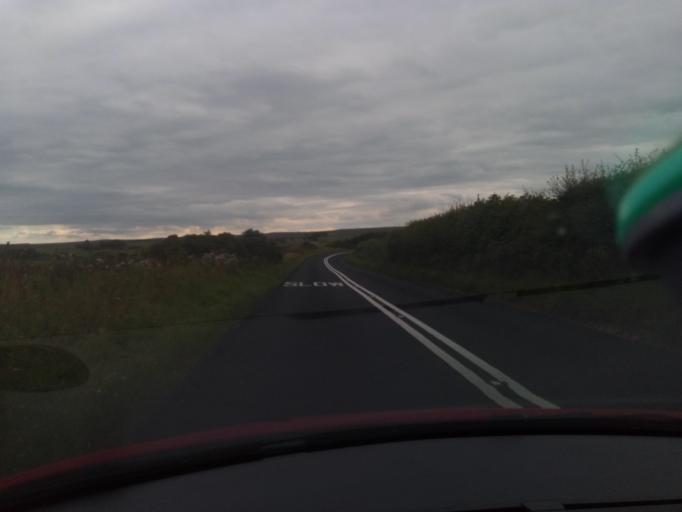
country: GB
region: England
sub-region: Northumberland
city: Warden
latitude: 54.9537
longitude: -2.1751
